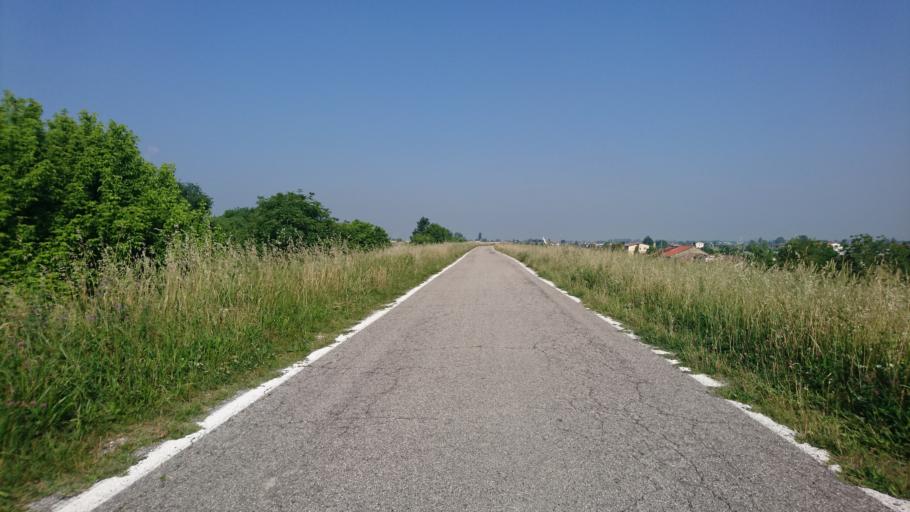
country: IT
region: Lombardy
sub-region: Provincia di Mantova
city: Borgofranco sul Po
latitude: 45.0580
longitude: 11.2196
